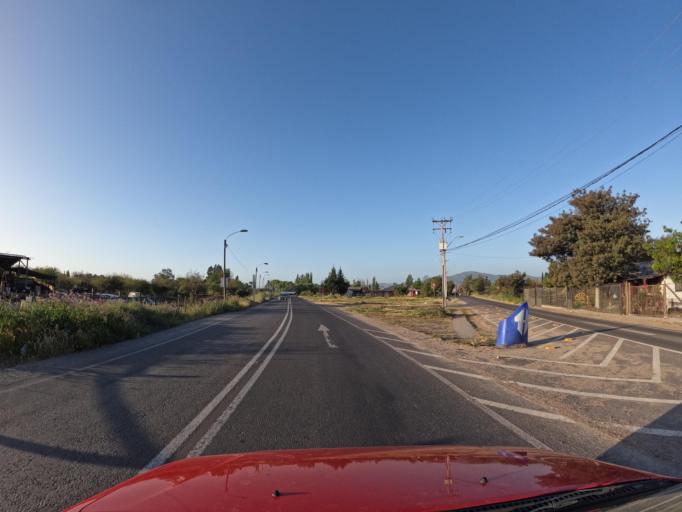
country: CL
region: O'Higgins
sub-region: Provincia de Colchagua
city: Santa Cruz
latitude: -34.3155
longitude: -71.3854
